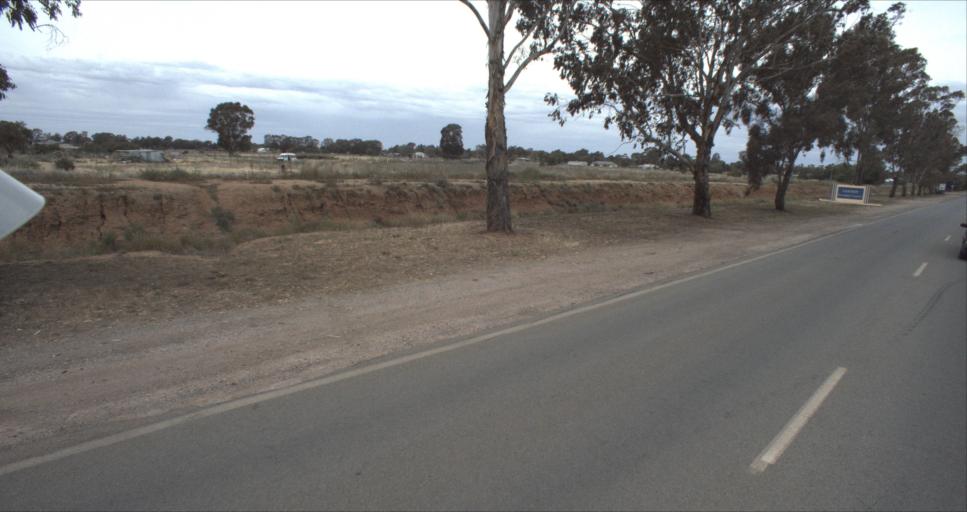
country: AU
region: New South Wales
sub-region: Leeton
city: Leeton
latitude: -34.5349
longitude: 146.4088
